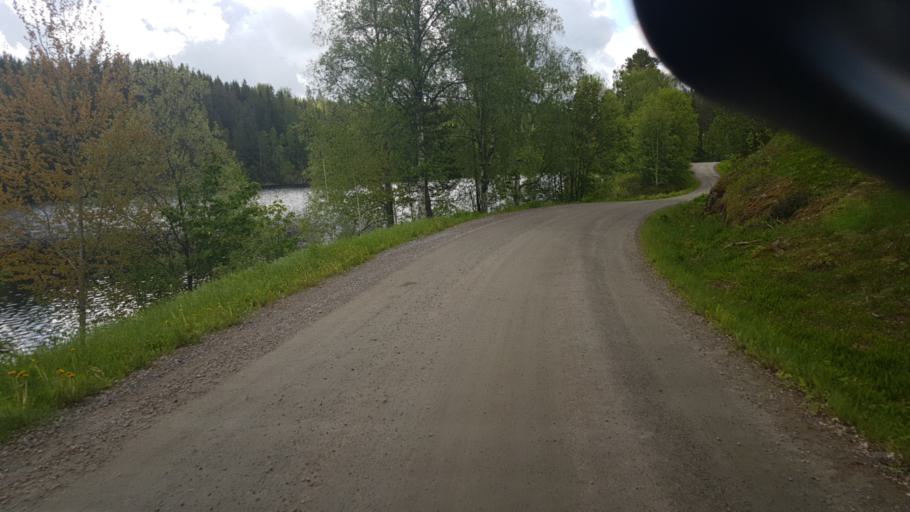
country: NO
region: Hedmark
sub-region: Eidskog
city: Skotterud
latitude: 59.8706
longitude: 11.9823
